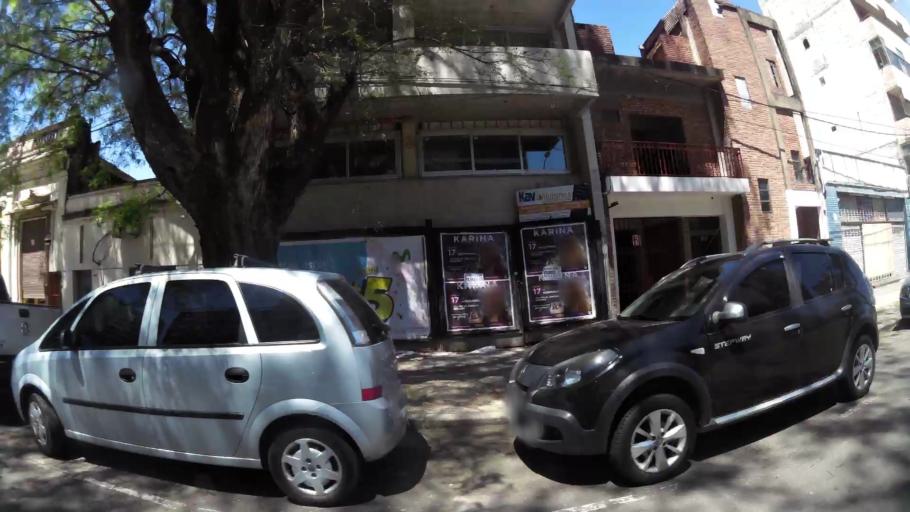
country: AR
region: Santa Fe
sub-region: Departamento de Rosario
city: Rosario
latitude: -32.9429
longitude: -60.6658
